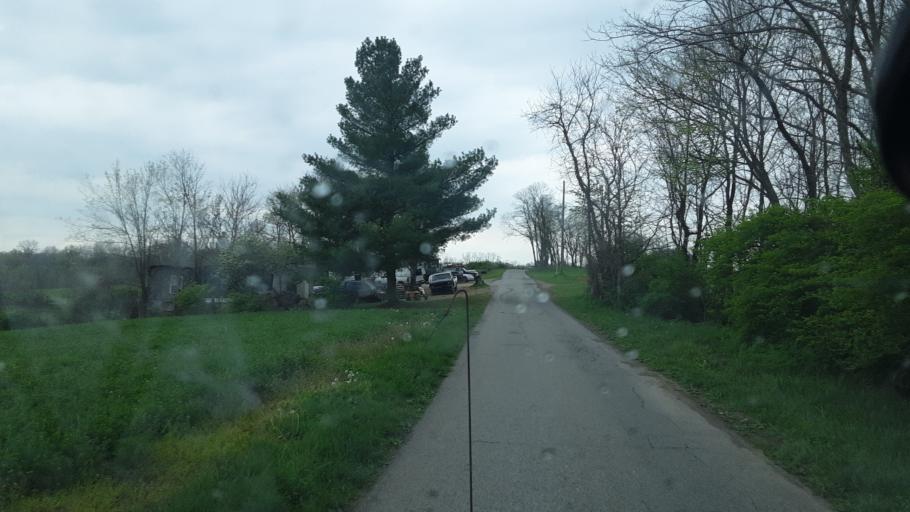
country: US
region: Kentucky
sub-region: Owen County
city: Owenton
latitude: 38.6750
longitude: -84.8048
